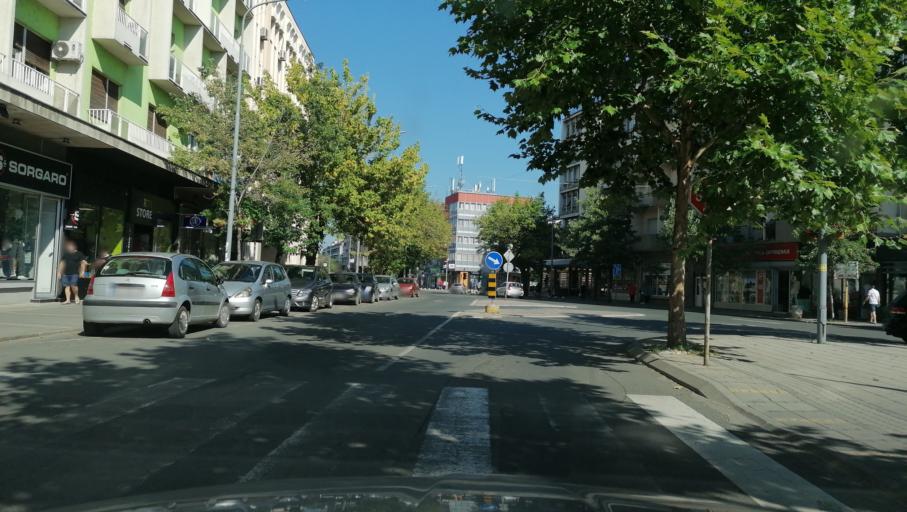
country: RS
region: Central Serbia
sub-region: Rasinski Okrug
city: Krusevac
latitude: 43.5797
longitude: 21.3308
